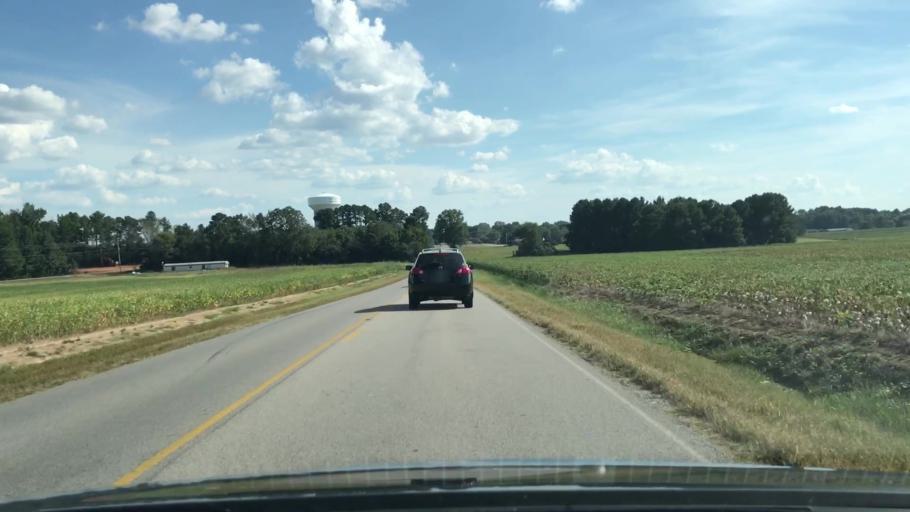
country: US
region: Alabama
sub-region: Madison County
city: Harvest
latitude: 34.8662
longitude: -86.7490
